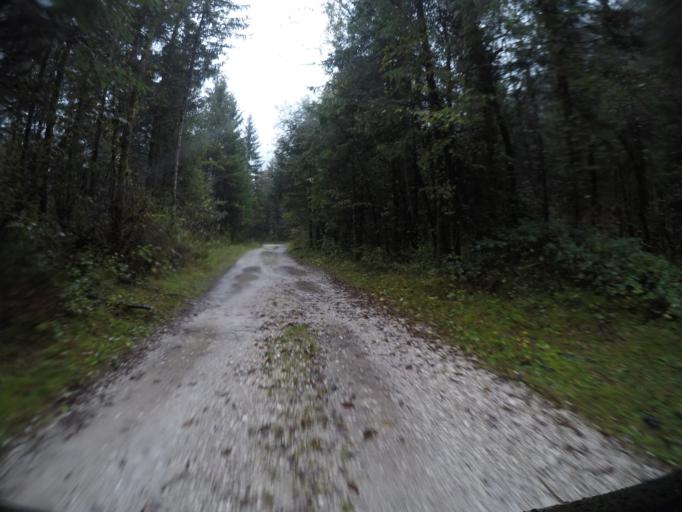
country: SI
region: Bovec
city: Bovec
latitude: 46.3344
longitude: 13.6344
